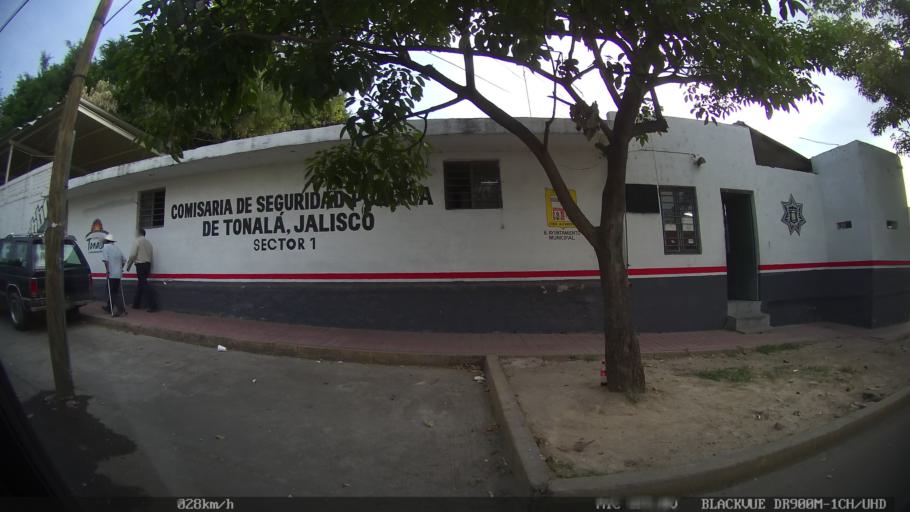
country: MX
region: Jalisco
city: Tonala
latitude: 20.6211
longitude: -103.2365
